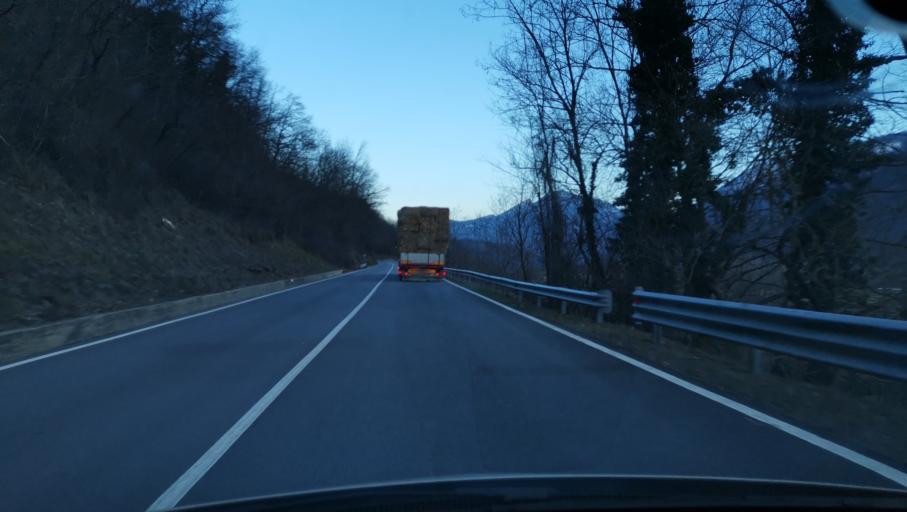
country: IT
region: Piedmont
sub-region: Provincia di Cuneo
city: Demonte
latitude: 44.3139
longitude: 7.2771
